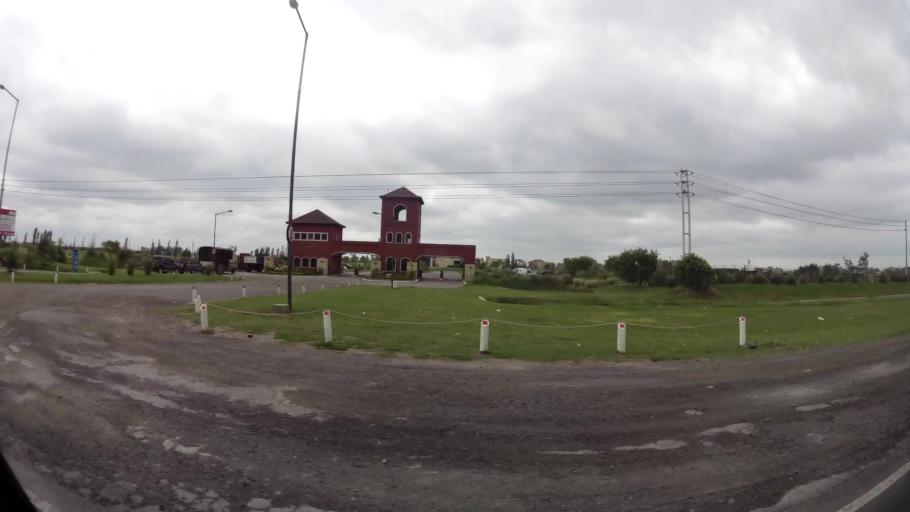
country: AR
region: Buenos Aires
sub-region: Partido de San Vicente
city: San Vicente
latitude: -34.9698
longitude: -58.4673
